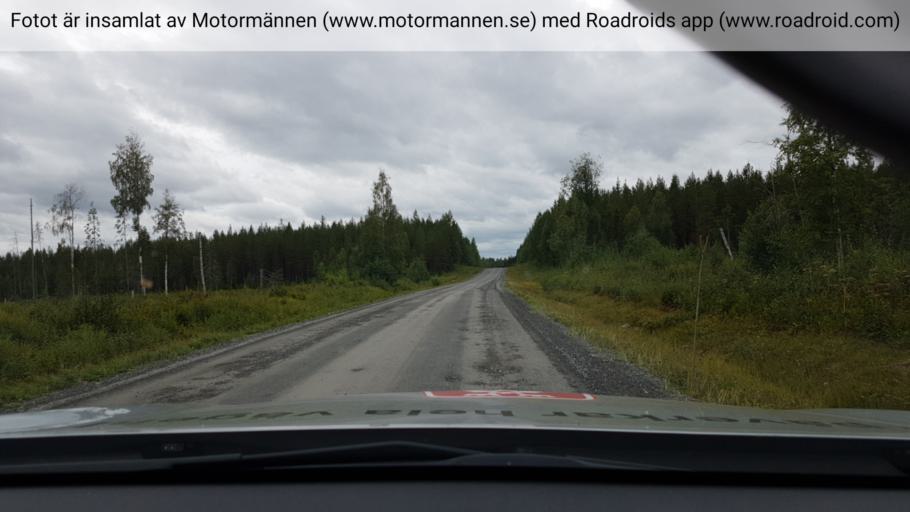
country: SE
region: Vaesterbotten
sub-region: Skelleftea Kommun
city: Forsbacka
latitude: 64.8221
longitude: 20.4964
